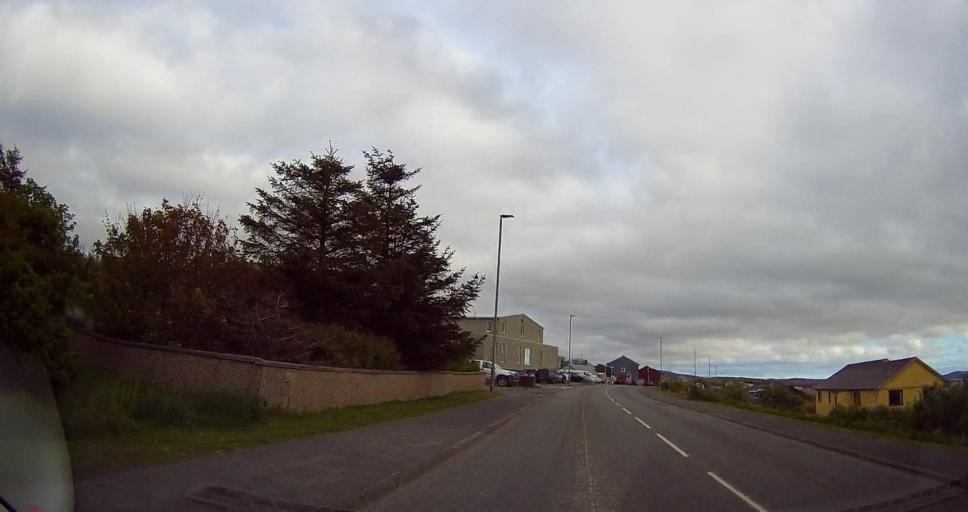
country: GB
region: Scotland
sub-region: Shetland Islands
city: Lerwick
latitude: 60.3928
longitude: -1.3499
